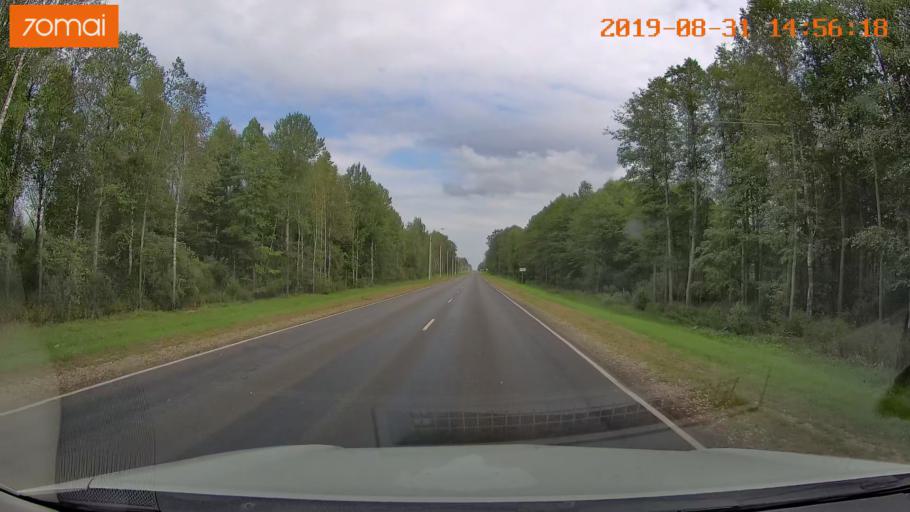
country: RU
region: Kaluga
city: Spas-Demensk
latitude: 54.3039
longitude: 33.9348
